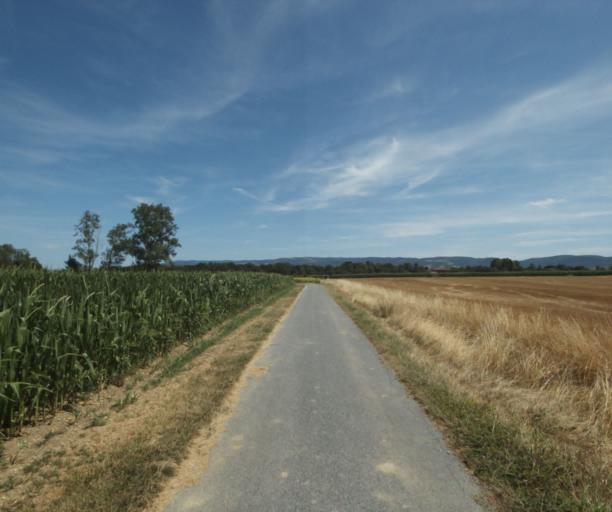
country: FR
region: Midi-Pyrenees
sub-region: Departement de la Haute-Garonne
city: Revel
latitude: 43.5085
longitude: 2.0182
